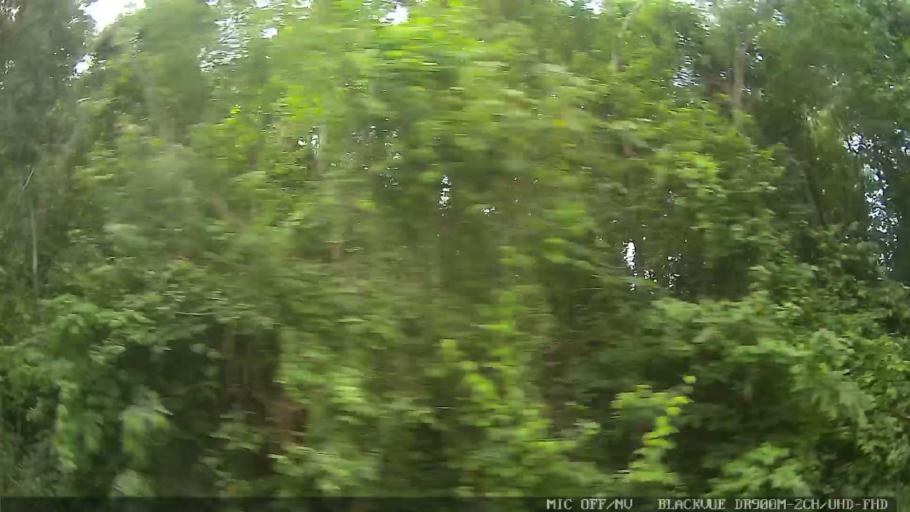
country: BR
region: Sao Paulo
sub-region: Amparo
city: Amparo
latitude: -22.7016
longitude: -46.7001
